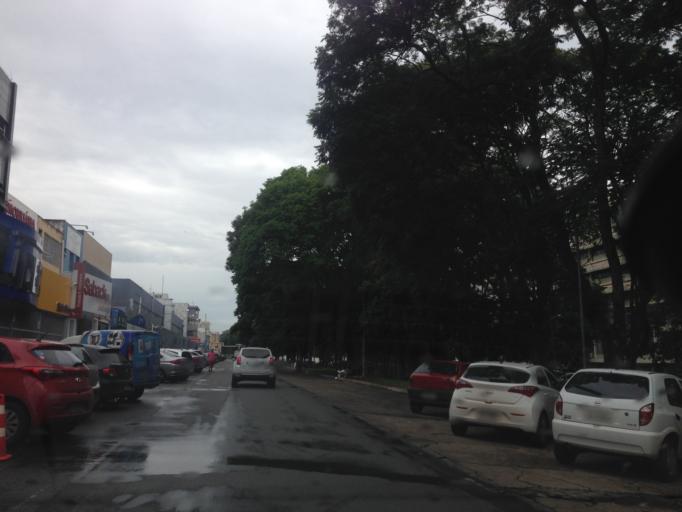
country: BR
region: Federal District
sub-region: Brasilia
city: Brasilia
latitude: -15.8082
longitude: -47.9000
